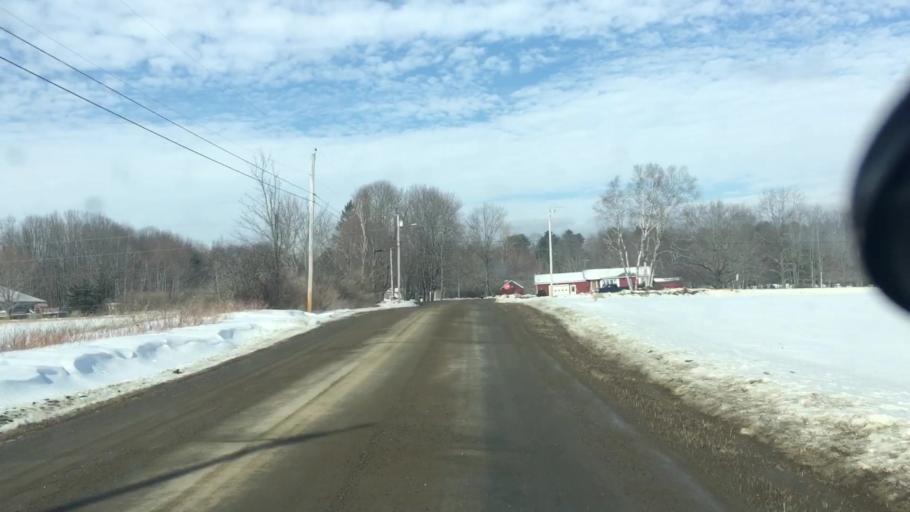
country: US
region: Maine
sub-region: Penobscot County
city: Levant
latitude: 44.8612
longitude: -68.8794
